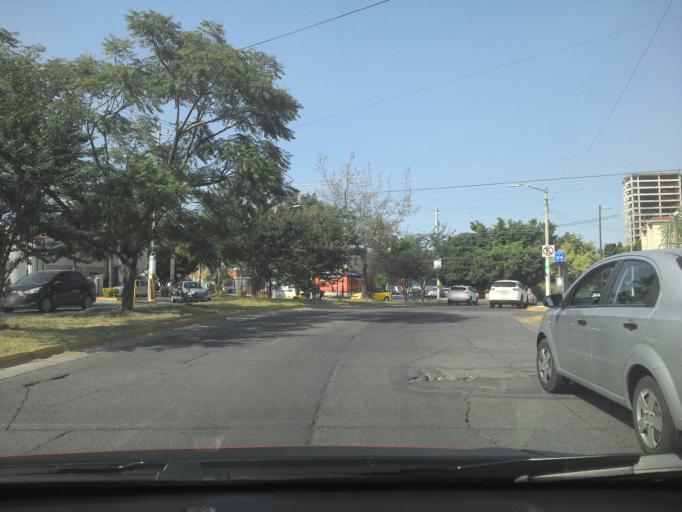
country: MX
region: Jalisco
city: Guadalajara
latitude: 20.6517
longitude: -103.4414
